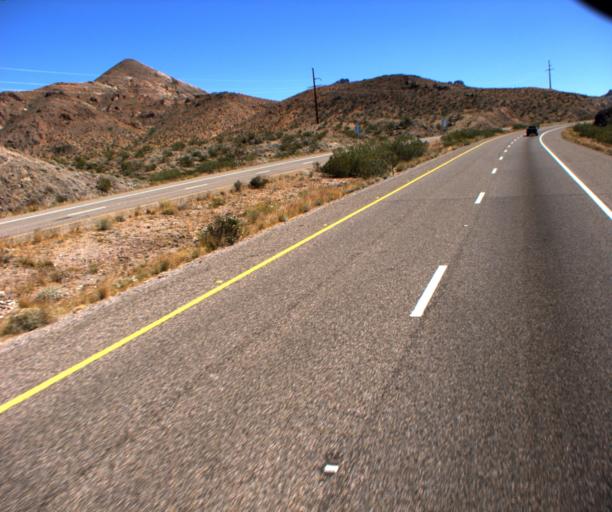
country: US
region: Nevada
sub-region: Clark County
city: Laughlin
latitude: 35.1936
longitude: -114.4402
